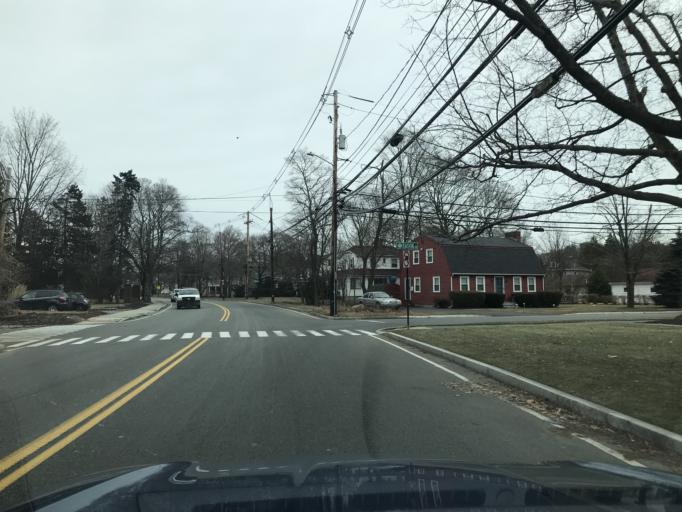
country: US
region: Massachusetts
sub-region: Essex County
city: Lynnfield
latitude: 42.5142
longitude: -71.0094
